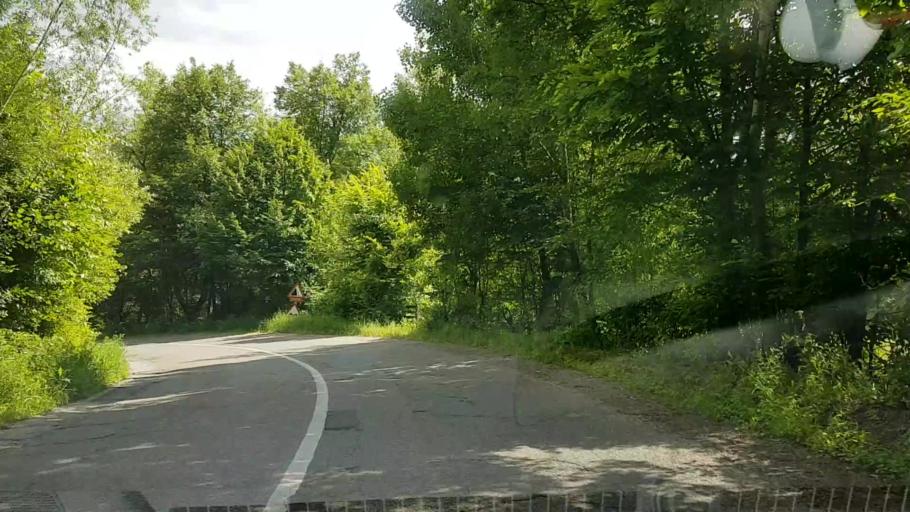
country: RO
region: Neamt
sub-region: Comuna Ceahlau
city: Ceahlau
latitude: 47.0584
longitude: 25.9696
